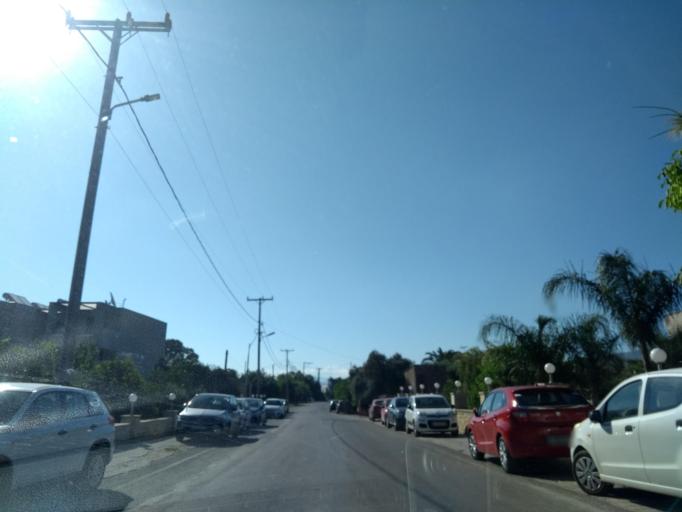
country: GR
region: Crete
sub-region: Nomos Chanias
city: Georgioupolis
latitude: 35.3674
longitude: 24.2543
